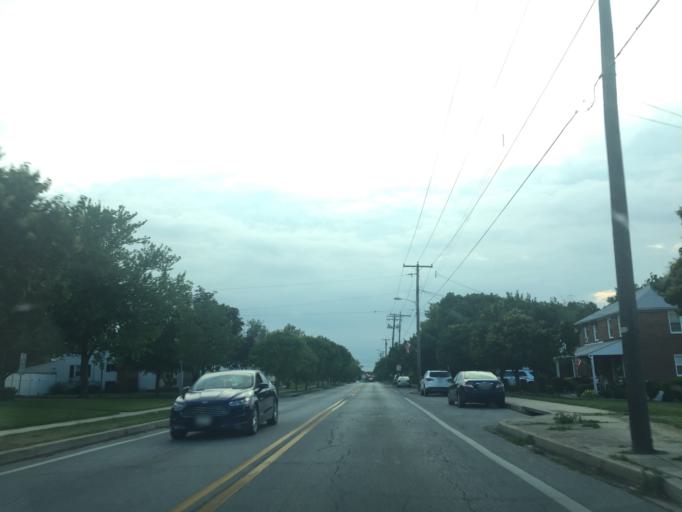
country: US
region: Maryland
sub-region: Anne Arundel County
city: Brooklyn Park
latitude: 39.2184
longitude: -76.6091
